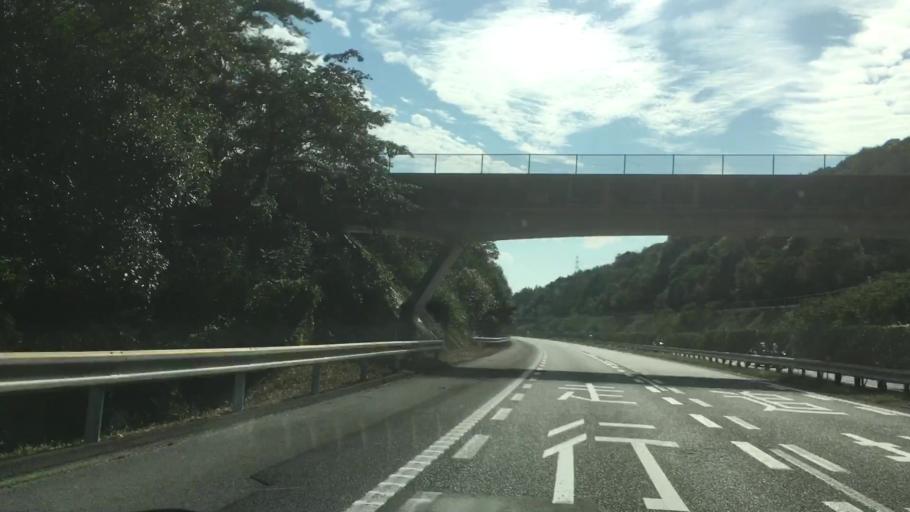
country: JP
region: Yamaguchi
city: Hikari
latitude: 34.0573
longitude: 132.0064
